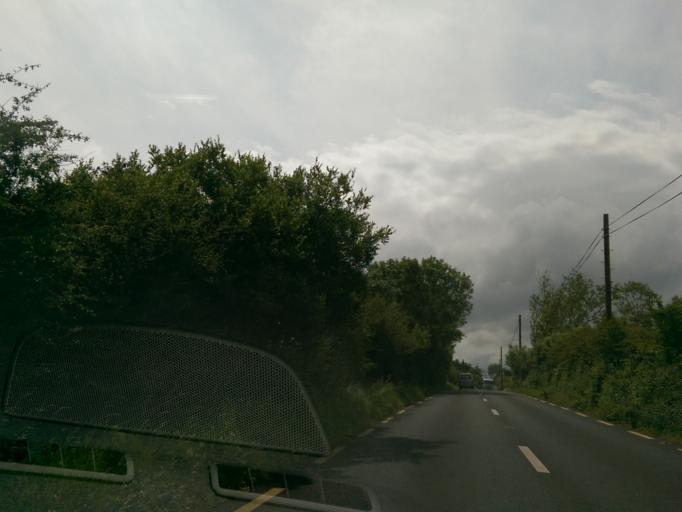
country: IE
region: Munster
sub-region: An Clar
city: Kilrush
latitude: 52.6940
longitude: -9.3444
